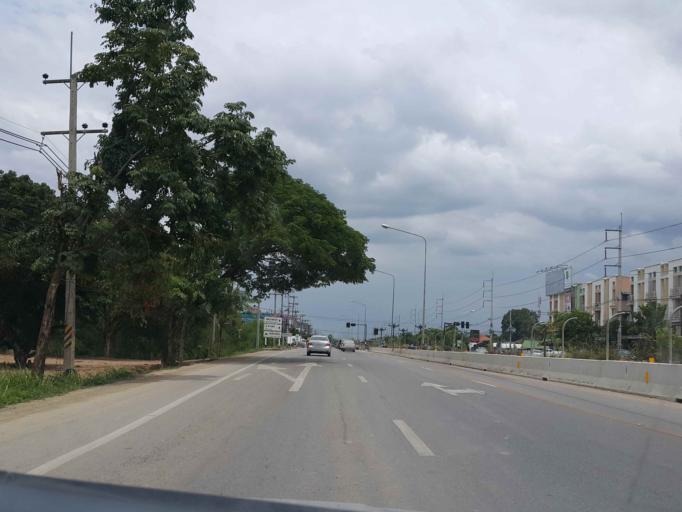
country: TH
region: Chiang Mai
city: Chiang Mai
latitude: 18.7509
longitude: 98.9410
